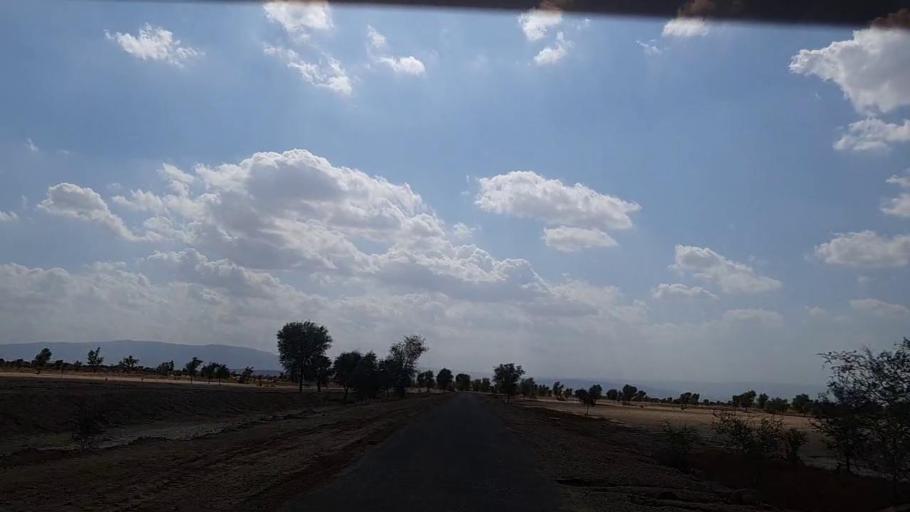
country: PK
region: Sindh
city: Johi
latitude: 26.5224
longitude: 67.4922
